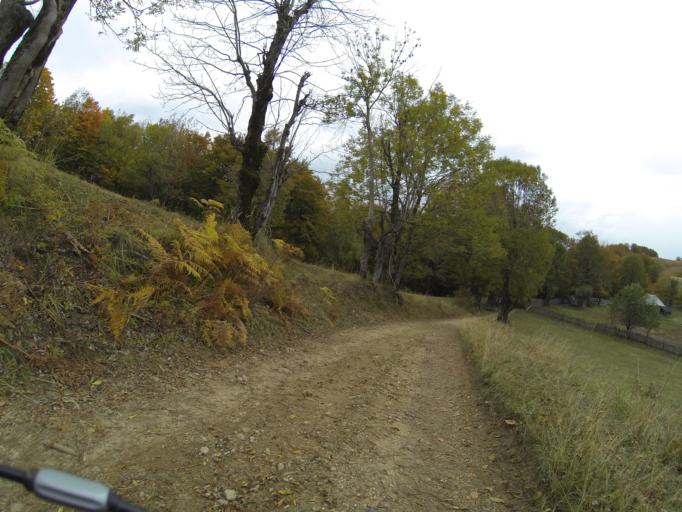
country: RO
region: Gorj
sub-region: Comuna Pades
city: Closani
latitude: 45.1090
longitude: 22.8460
